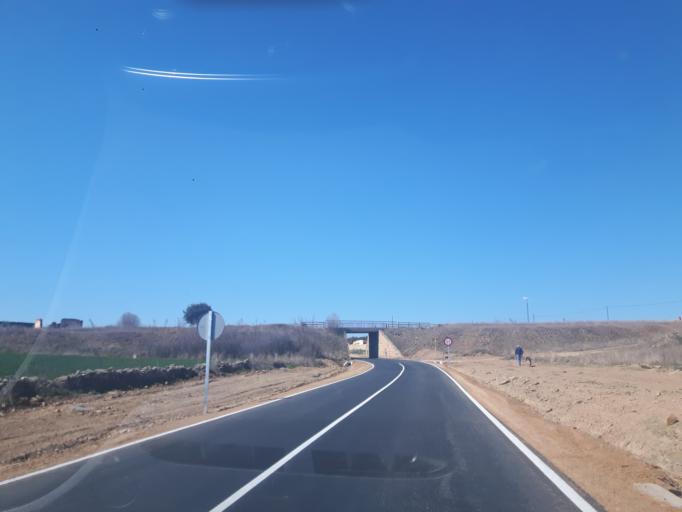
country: ES
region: Castille and Leon
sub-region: Provincia de Salamanca
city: Alba de Tormes
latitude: 40.8237
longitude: -5.5273
